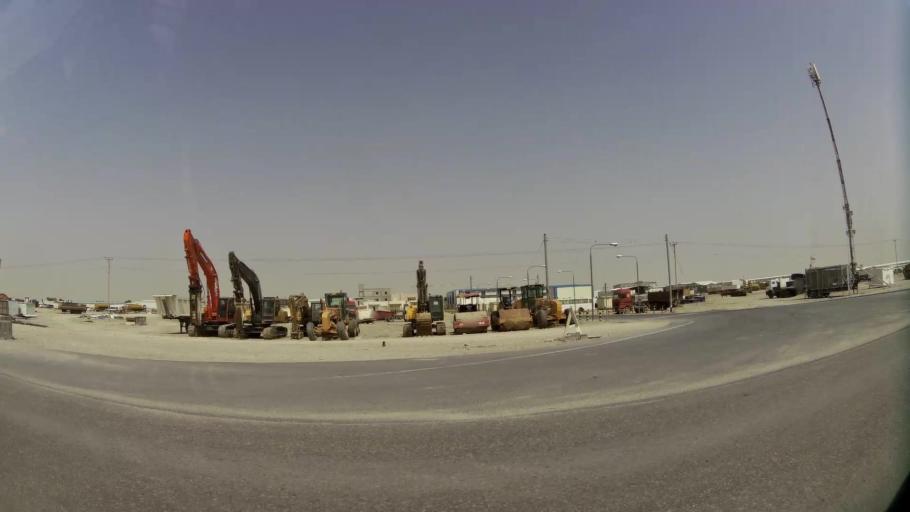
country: QA
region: Baladiyat ar Rayyan
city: Ar Rayyan
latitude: 25.2134
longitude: 51.3573
